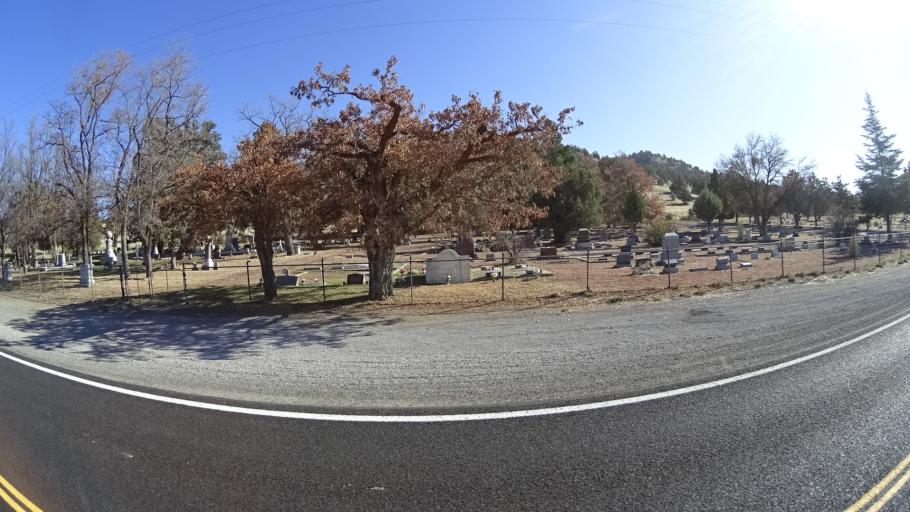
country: US
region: California
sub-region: Siskiyou County
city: Montague
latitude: 41.7096
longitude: -122.3793
